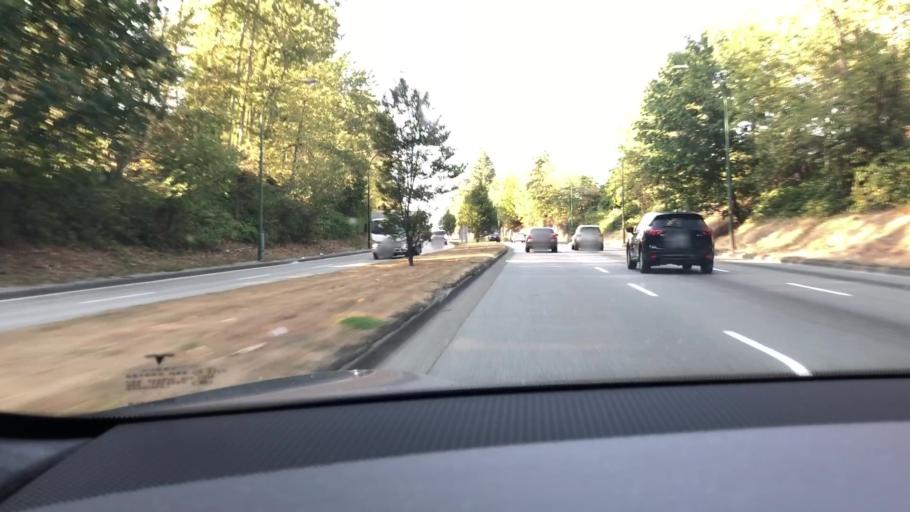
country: CA
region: British Columbia
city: Burnaby
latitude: 49.2113
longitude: -123.0238
